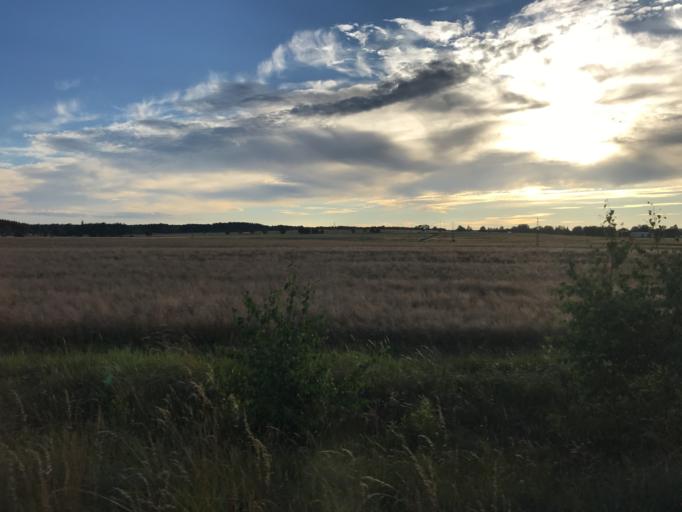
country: CZ
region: Jihocesky
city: Suchdol nad Luznici
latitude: 48.8839
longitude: 14.8786
